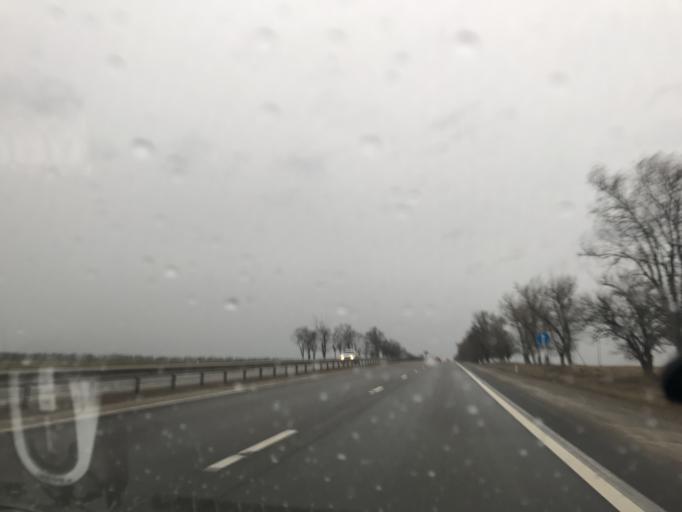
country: RU
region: Krasnodarskiy
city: Pavlovskaya
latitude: 46.1512
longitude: 39.8488
